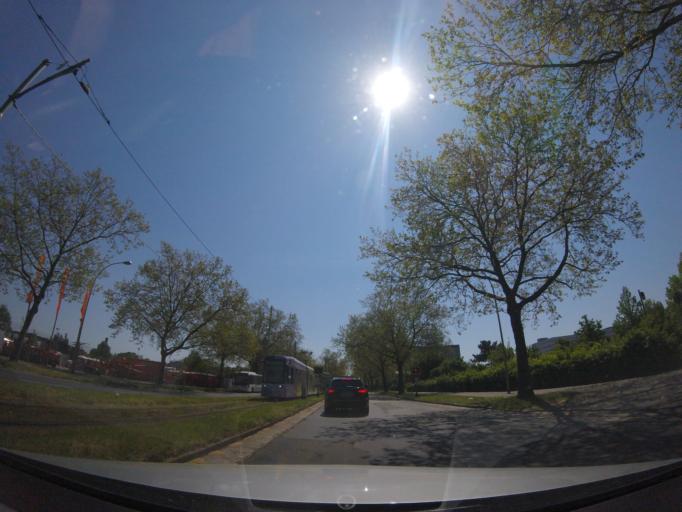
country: DE
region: Hesse
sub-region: Regierungsbezirk Darmstadt
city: Offenbach
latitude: 50.1267
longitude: 8.7554
